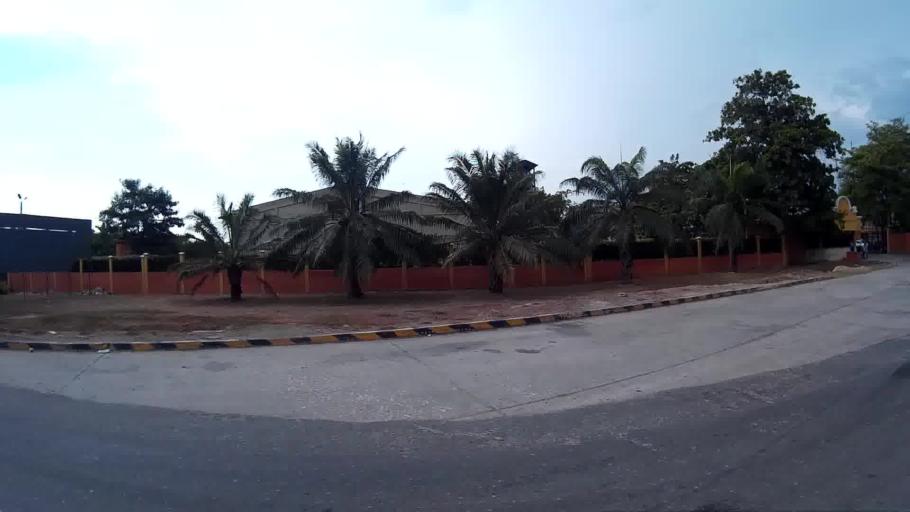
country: CO
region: Magdalena
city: Cienaga
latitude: 11.0038
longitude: -74.2221
